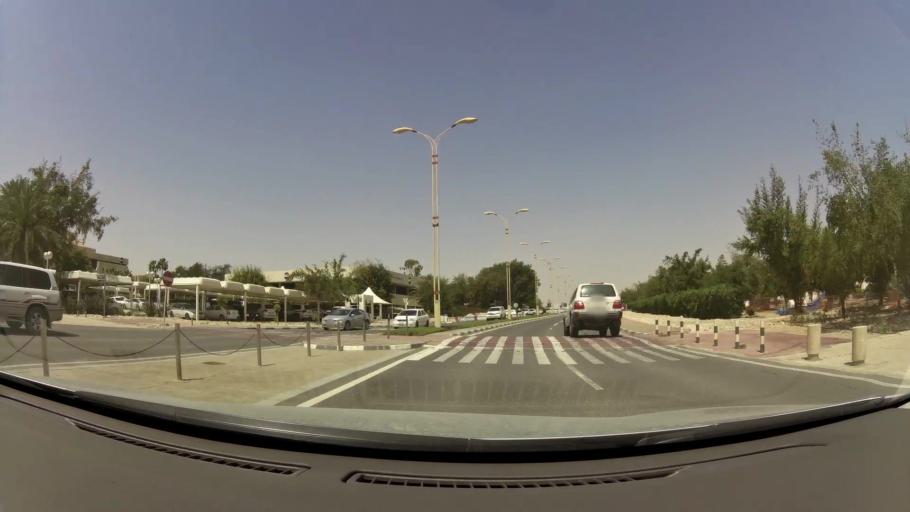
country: QA
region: Baladiyat ad Dawhah
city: Doha
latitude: 25.3741
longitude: 51.4939
